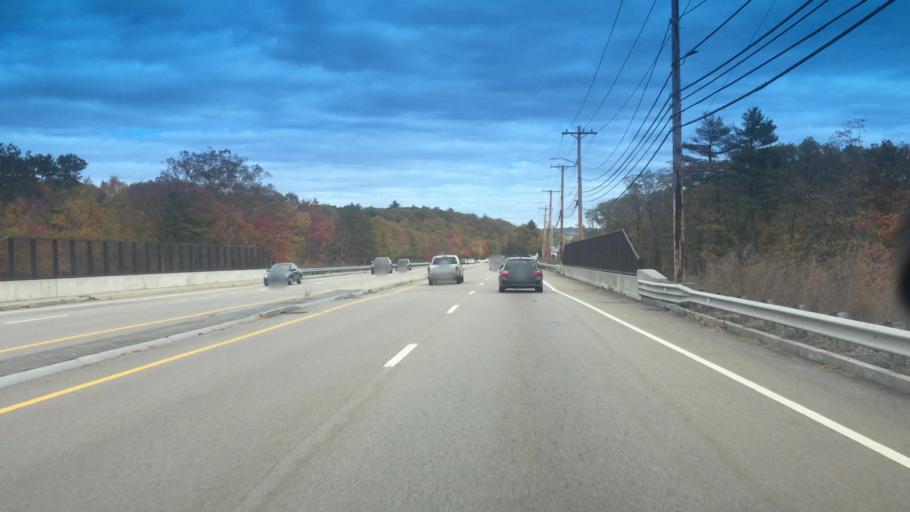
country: US
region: Massachusetts
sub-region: Norfolk County
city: Westwood
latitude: 42.2430
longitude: -71.2058
